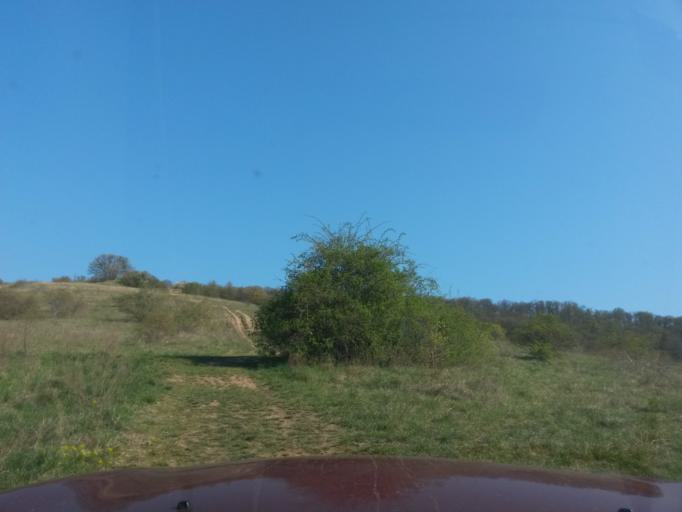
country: SK
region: Kosicky
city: Kosice
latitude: 48.7555
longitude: 21.2405
